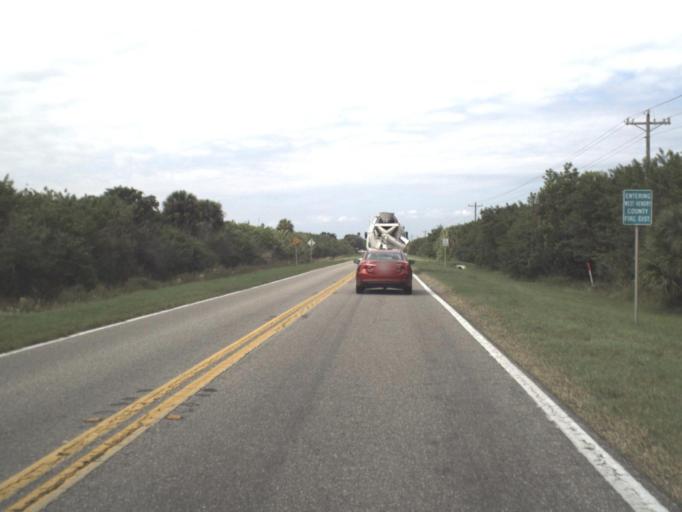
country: US
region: Florida
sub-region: Glades County
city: Moore Haven
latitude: 26.7682
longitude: -81.1752
